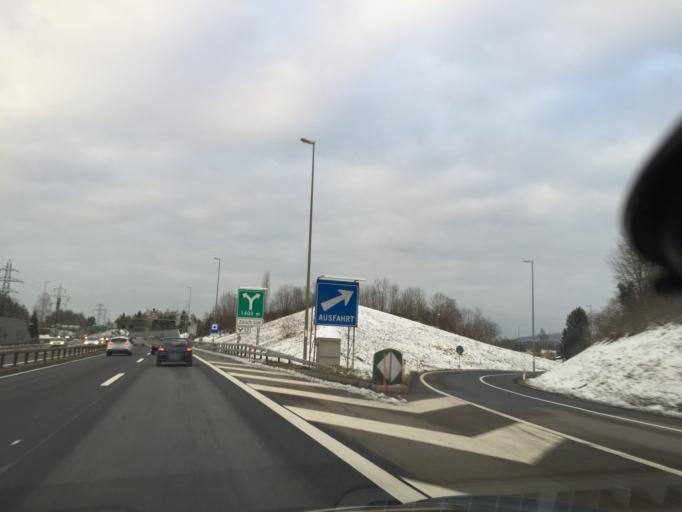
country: CH
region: Zurich
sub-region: Bezirk Horgen
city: Kilchberg / Baechler-Stocken
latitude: 47.3276
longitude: 8.5309
